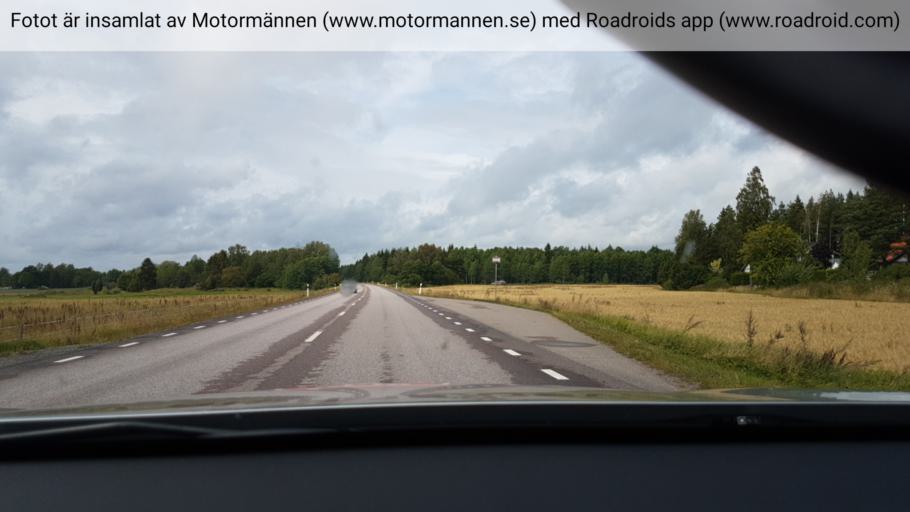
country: SE
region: Uppsala
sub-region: Osthammars Kommun
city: Bjorklinge
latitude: 59.9565
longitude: 17.4013
